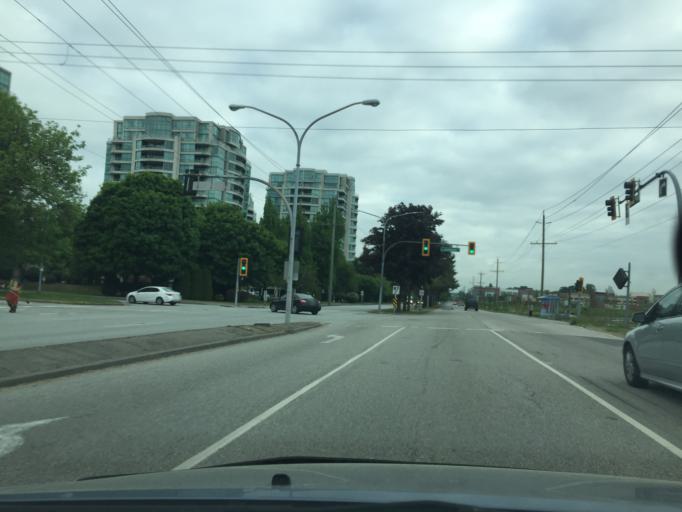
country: CA
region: British Columbia
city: Richmond
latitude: 49.1734
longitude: -123.1246
